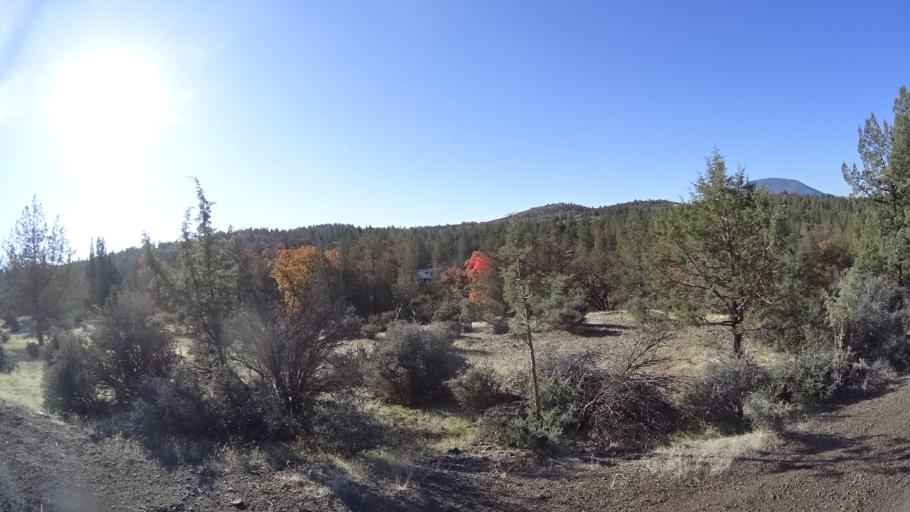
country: US
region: California
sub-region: Siskiyou County
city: Montague
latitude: 41.9130
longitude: -122.4297
